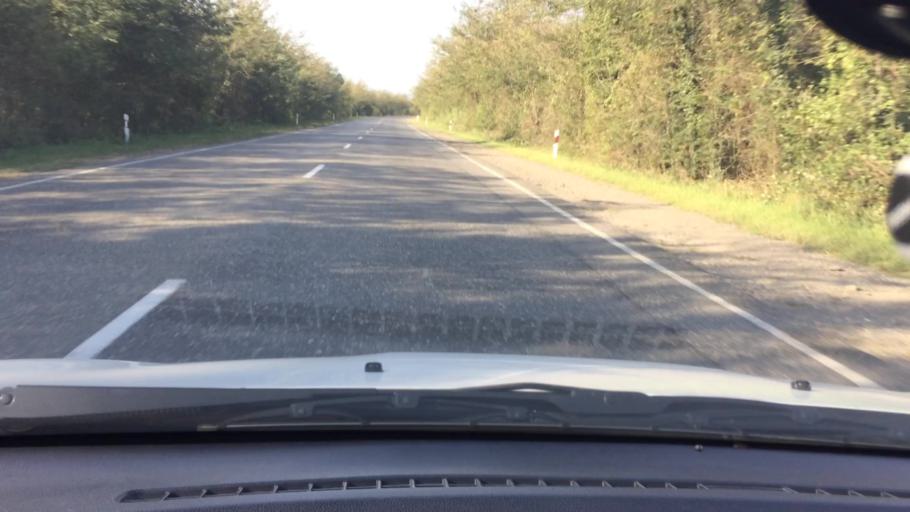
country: GE
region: Imereti
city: Vani
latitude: 42.2001
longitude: 42.5291
